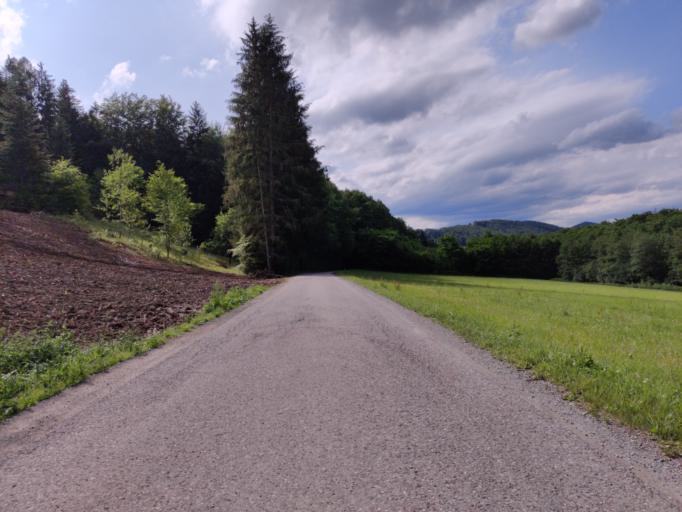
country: AT
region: Styria
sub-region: Politischer Bezirk Graz-Umgebung
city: Thal
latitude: 47.0639
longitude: 15.3430
